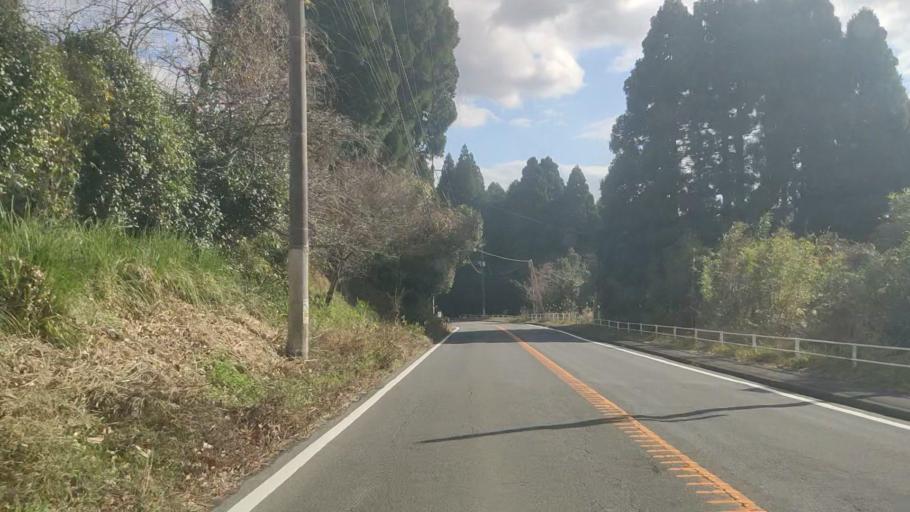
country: JP
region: Kagoshima
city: Kajiki
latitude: 31.8245
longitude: 130.6912
